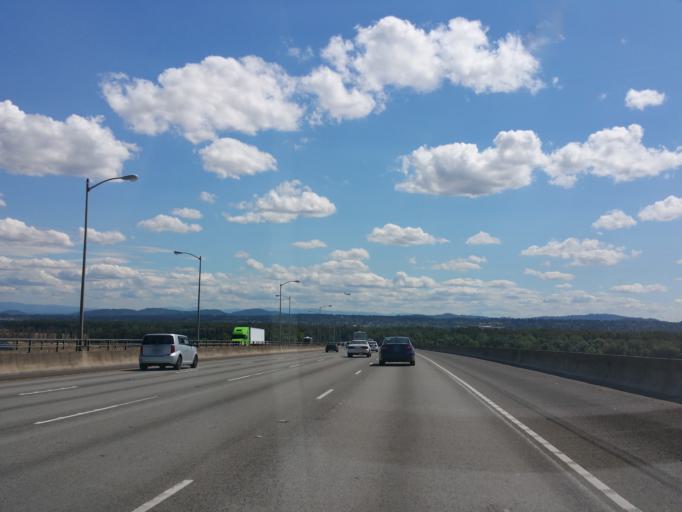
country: US
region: Washington
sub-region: Clark County
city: Orchards
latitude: 45.5963
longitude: -122.5500
